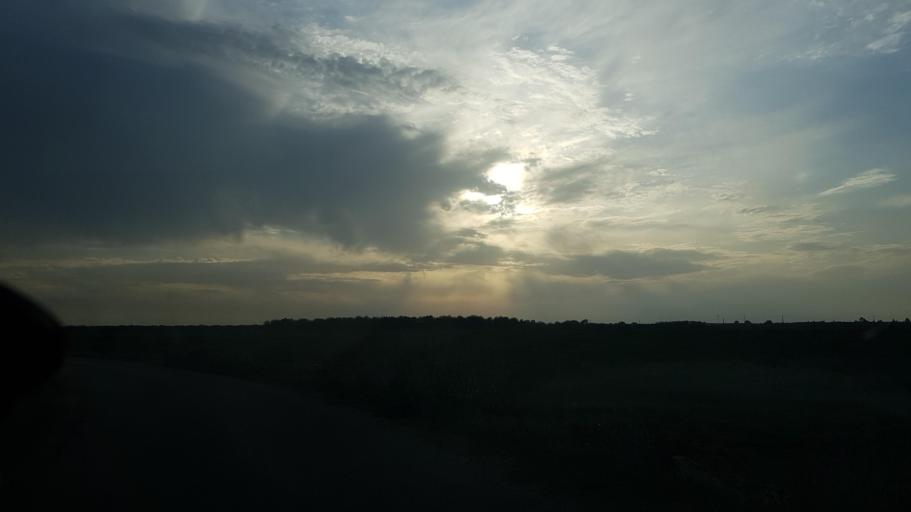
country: IT
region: Apulia
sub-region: Provincia di Brindisi
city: Mesagne
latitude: 40.5247
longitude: 17.8320
